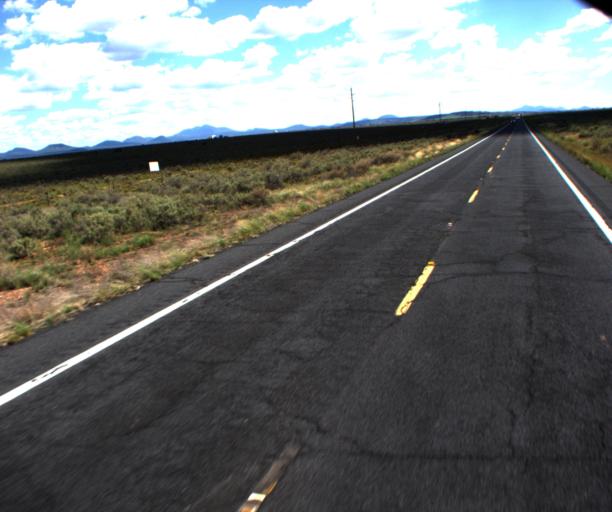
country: US
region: Arizona
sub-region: Coconino County
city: Williams
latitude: 35.6214
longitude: -112.1437
